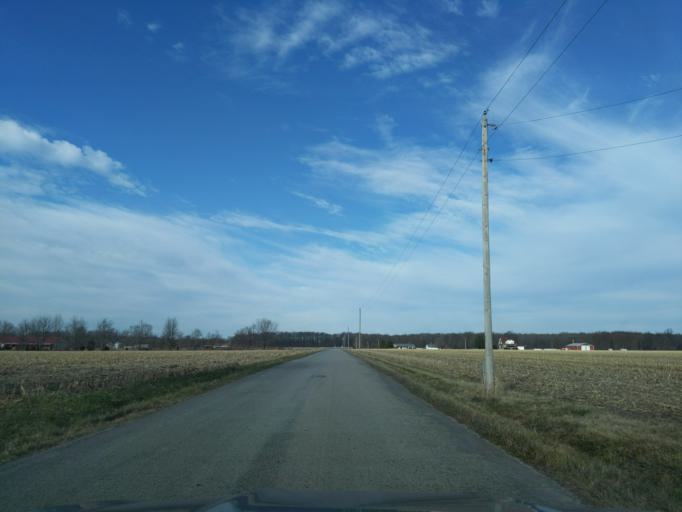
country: US
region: Indiana
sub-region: Decatur County
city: Greensburg
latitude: 39.2600
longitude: -85.4189
